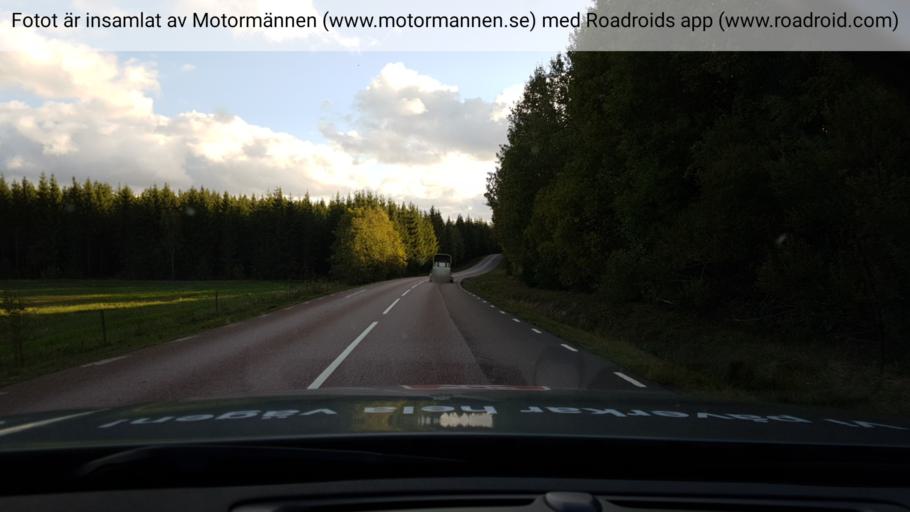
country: SE
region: Vaermland
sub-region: Karlstads Kommun
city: Molkom
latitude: 59.5462
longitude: 13.7823
